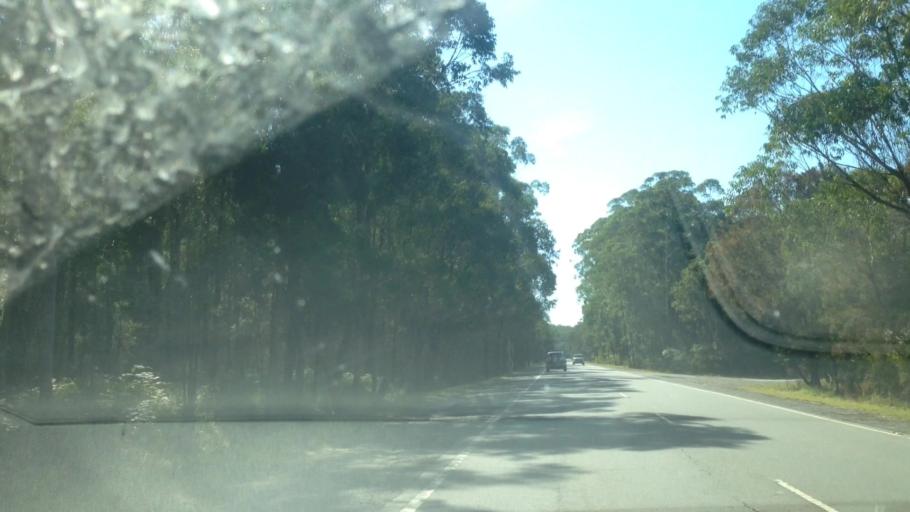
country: AU
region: New South Wales
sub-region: Lake Macquarie Shire
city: Toronto
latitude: -32.9874
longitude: 151.5079
